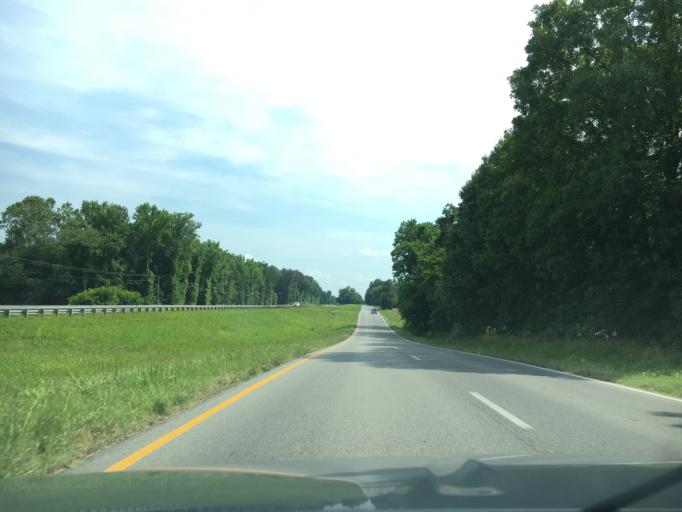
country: US
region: Virginia
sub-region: Nottoway County
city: Crewe
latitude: 37.2491
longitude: -78.1421
